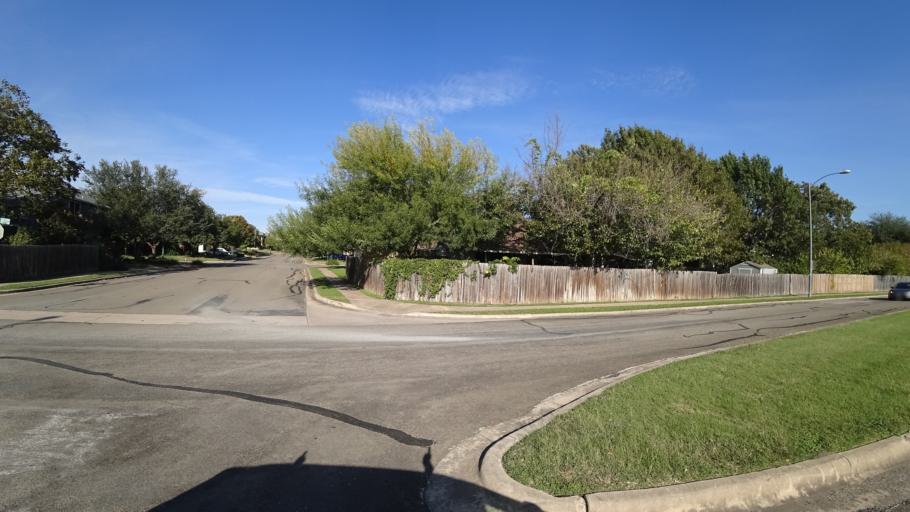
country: US
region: Texas
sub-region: Travis County
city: Pflugerville
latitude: 30.4027
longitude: -97.6493
